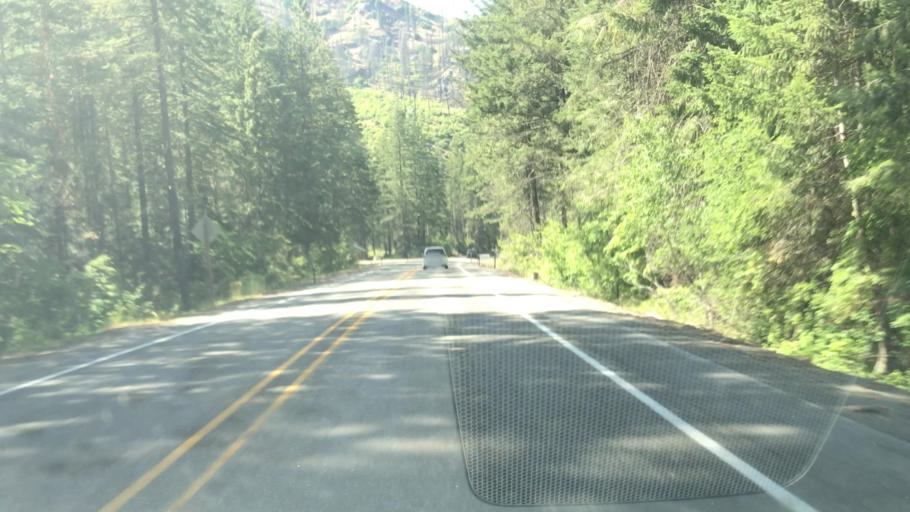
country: US
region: Washington
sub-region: Chelan County
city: Leavenworth
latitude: 47.6535
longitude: -120.7275
